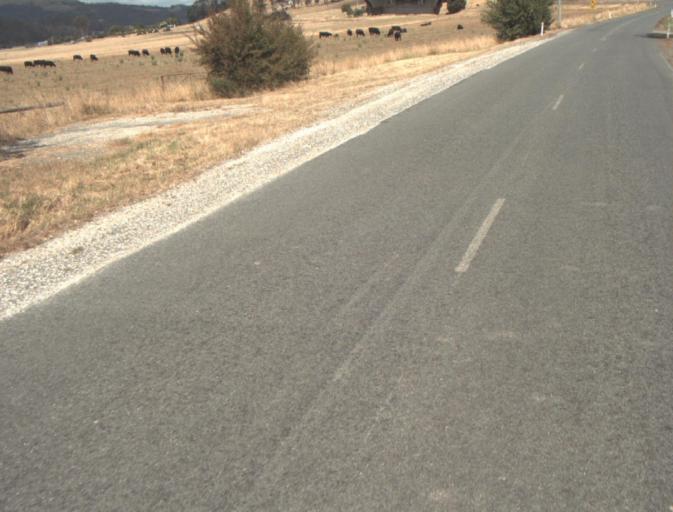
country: AU
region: Tasmania
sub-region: Launceston
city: Mayfield
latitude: -41.2318
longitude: 147.1249
